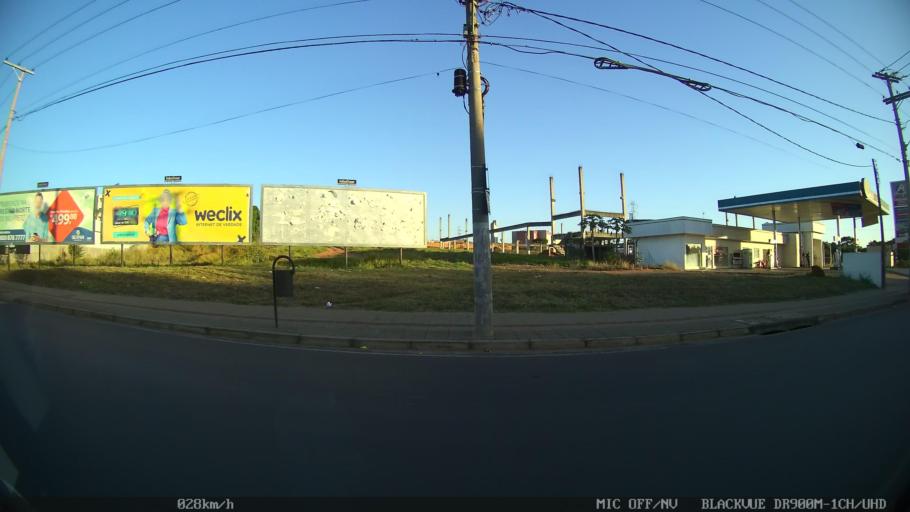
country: BR
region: Sao Paulo
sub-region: Sao Jose Do Rio Preto
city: Sao Jose do Rio Preto
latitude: -20.7837
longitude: -49.3808
